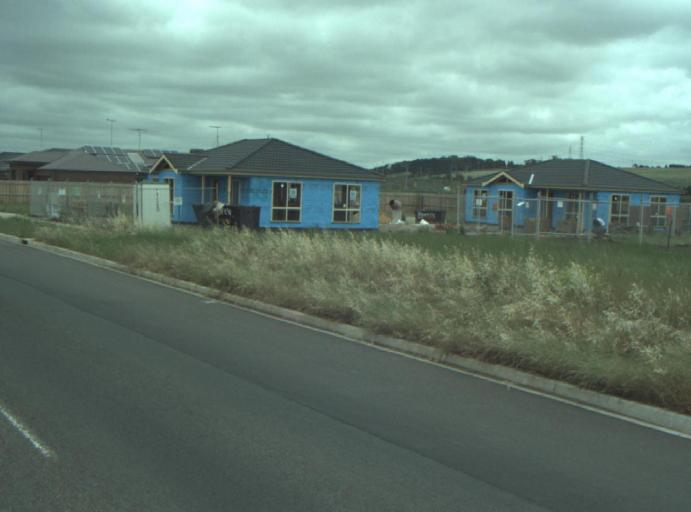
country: AU
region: Victoria
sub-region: Greater Geelong
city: Bell Post Hill
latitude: -38.0726
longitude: 144.3389
